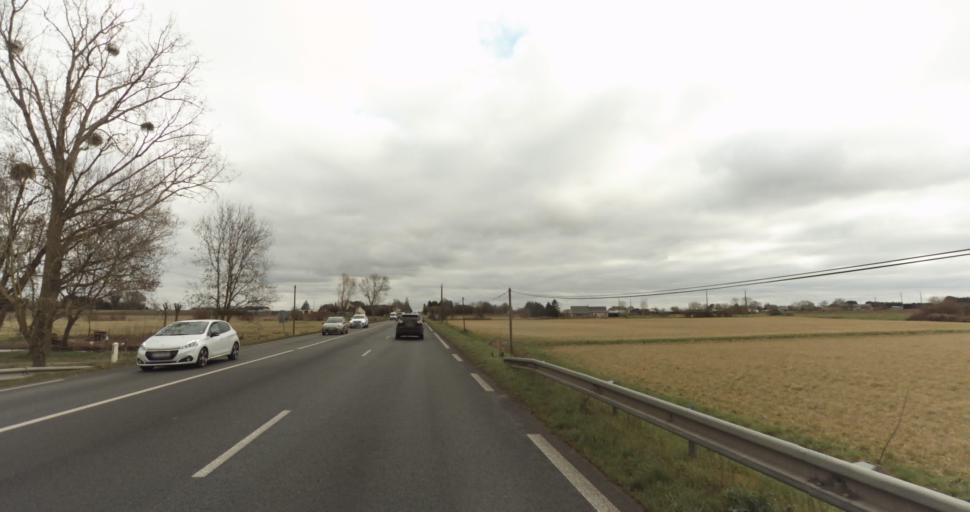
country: FR
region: Pays de la Loire
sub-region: Departement de Maine-et-Loire
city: Vivy
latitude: 47.3643
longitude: -0.0928
